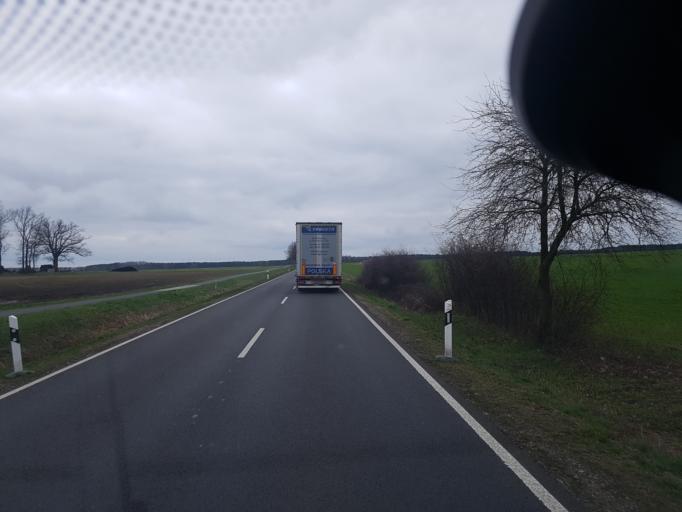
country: DE
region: Brandenburg
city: Tauche
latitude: 52.0804
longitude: 14.1613
